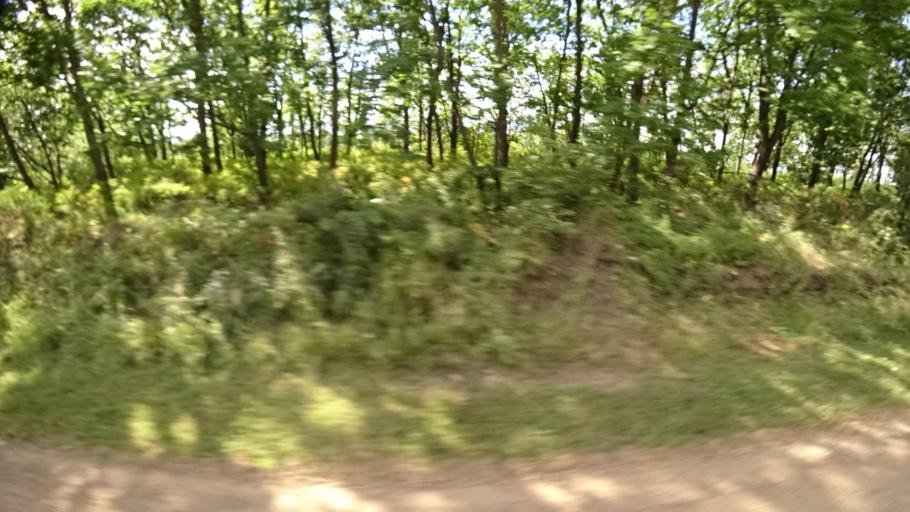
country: RU
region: Primorskiy
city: Yakovlevka
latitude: 44.4124
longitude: 133.5697
